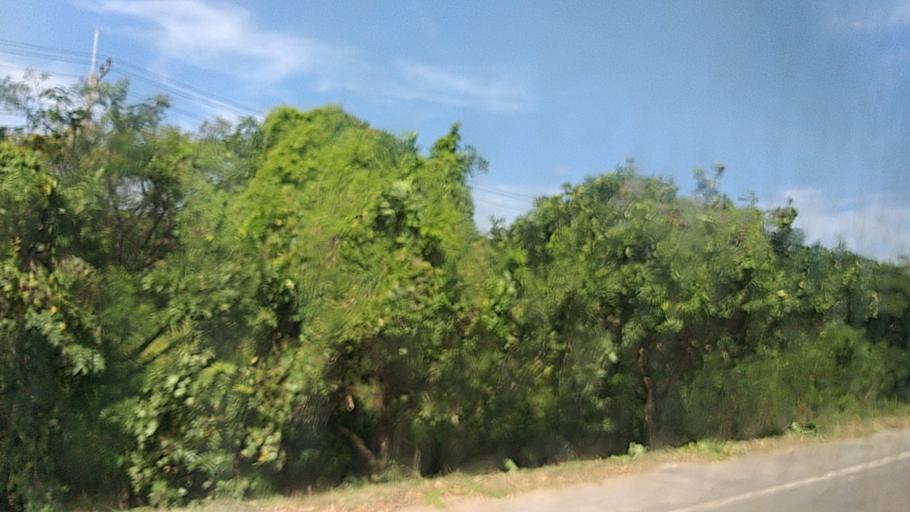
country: TH
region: Khon Kaen
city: Khon Kaen
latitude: 16.4342
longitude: 102.9176
